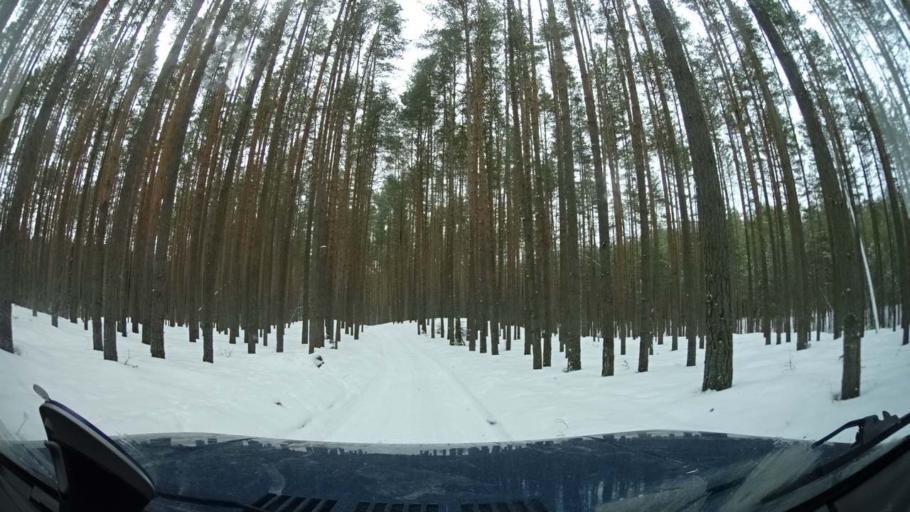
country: RU
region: Tverskaya
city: Radchenko
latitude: 56.6744
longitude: 36.4577
